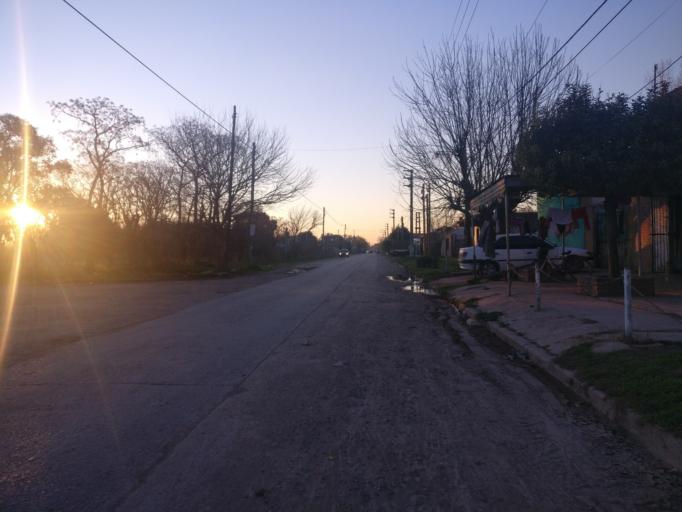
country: AR
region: Buenos Aires
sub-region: Partido de Ezeiza
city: Ezeiza
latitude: -34.9446
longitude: -58.6137
